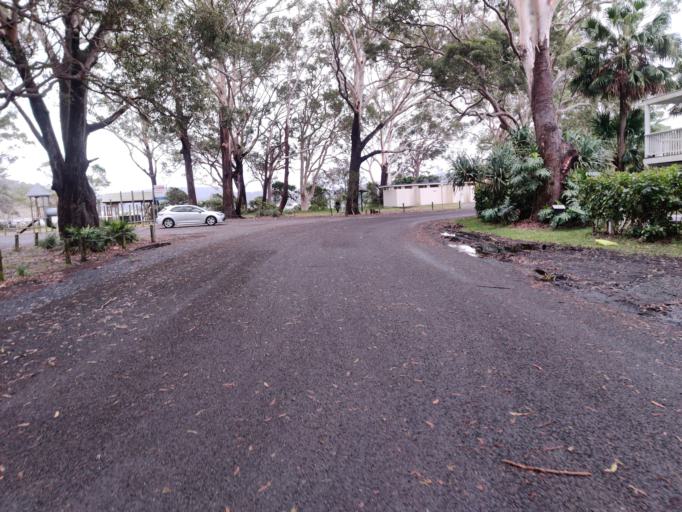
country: AU
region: New South Wales
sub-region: Great Lakes
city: Forster
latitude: -32.3900
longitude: 152.5020
